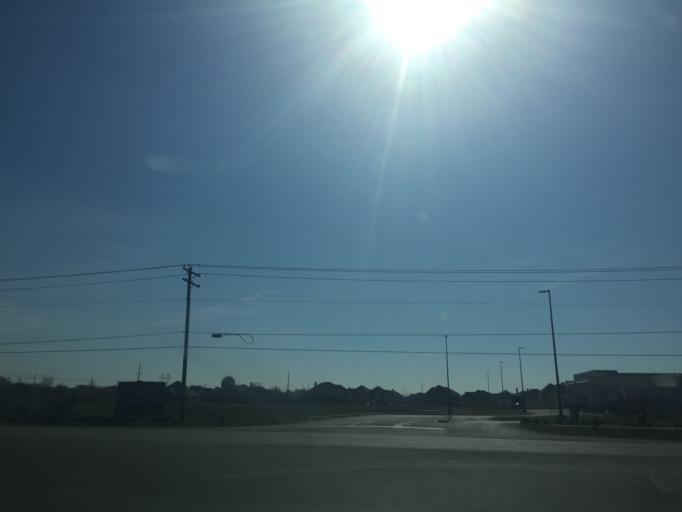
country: US
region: Texas
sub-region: Galveston County
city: Kemah
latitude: 29.5072
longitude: -95.0391
